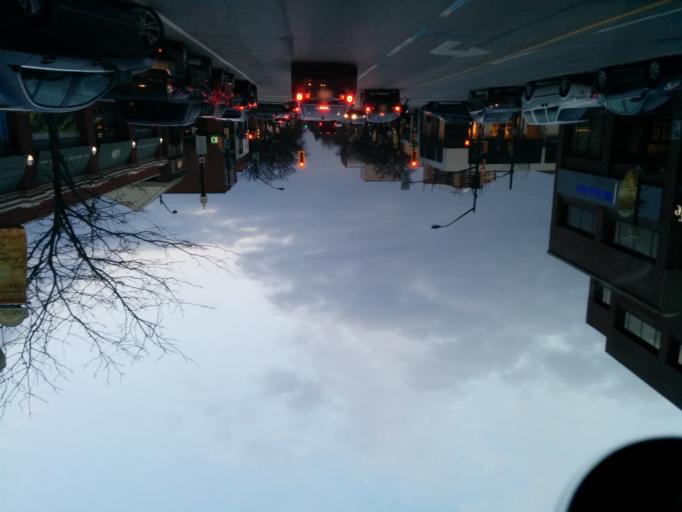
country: CA
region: Ontario
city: Oakville
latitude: 43.4470
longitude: -79.6669
